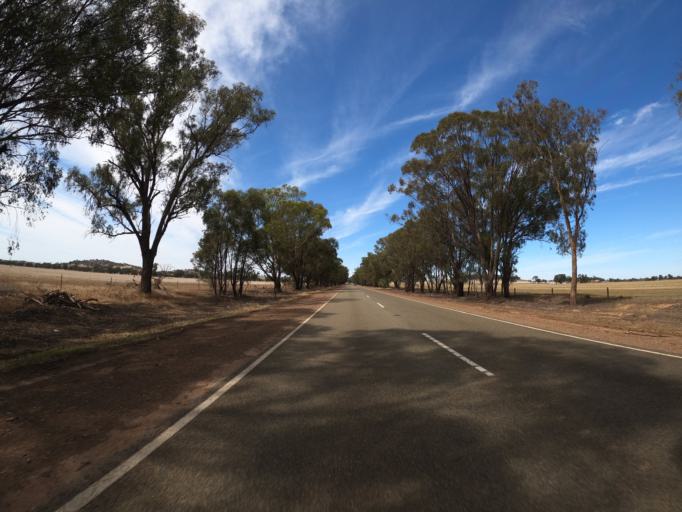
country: AU
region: Victoria
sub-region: Benalla
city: Benalla
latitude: -36.3112
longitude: 145.9583
